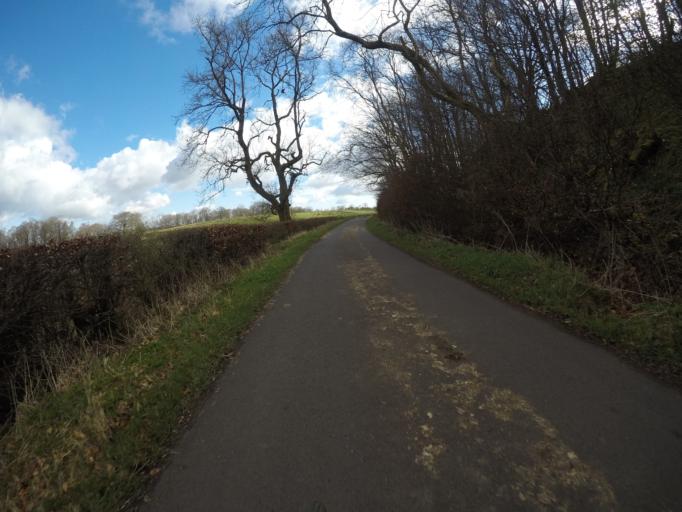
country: GB
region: Scotland
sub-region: North Ayrshire
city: Beith
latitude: 55.7153
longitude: -4.6442
